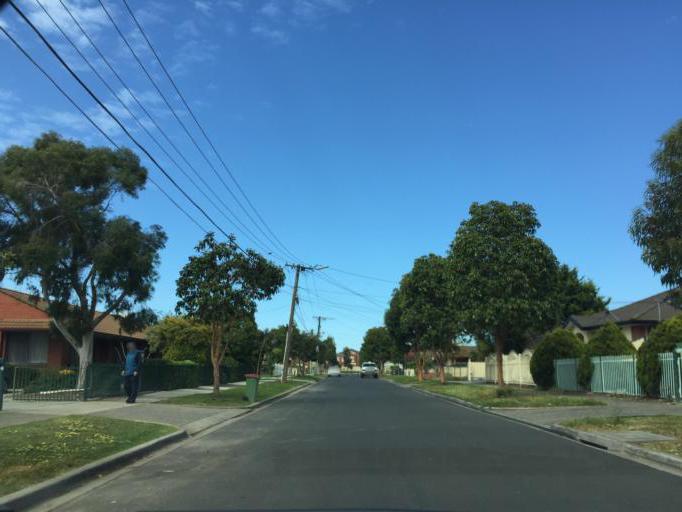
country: AU
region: Victoria
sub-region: Maribyrnong
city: Braybrook
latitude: -37.7884
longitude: 144.8565
